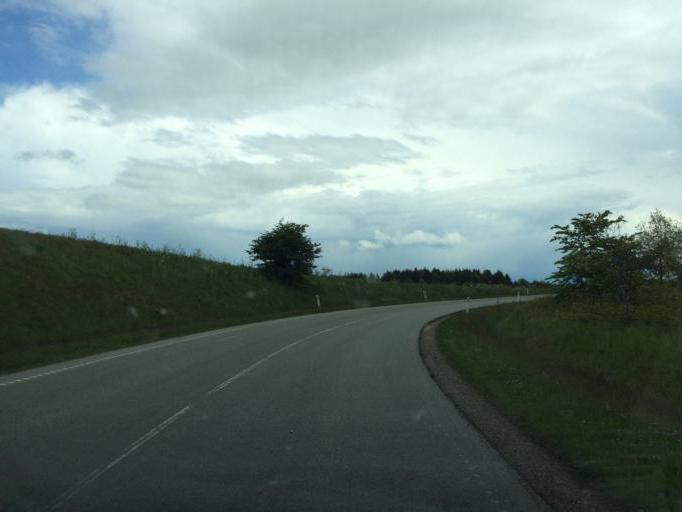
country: DK
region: North Denmark
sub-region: Vesthimmerland Kommune
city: Farso
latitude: 56.7161
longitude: 9.2707
